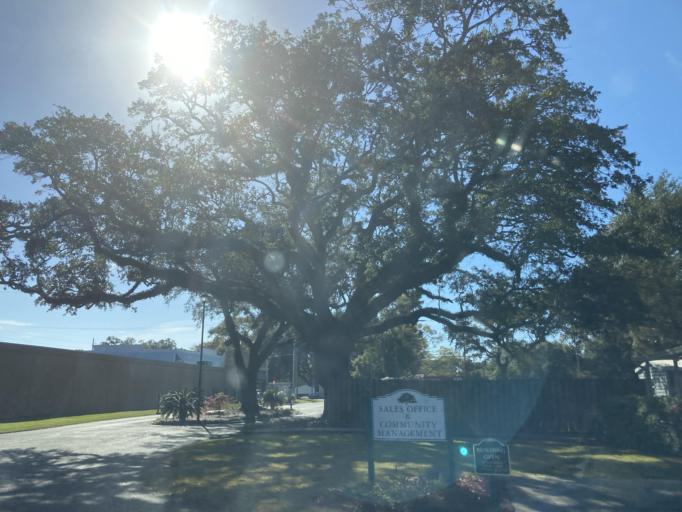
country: US
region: Mississippi
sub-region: Harrison County
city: D'Iberville
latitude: 30.4038
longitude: -88.9401
